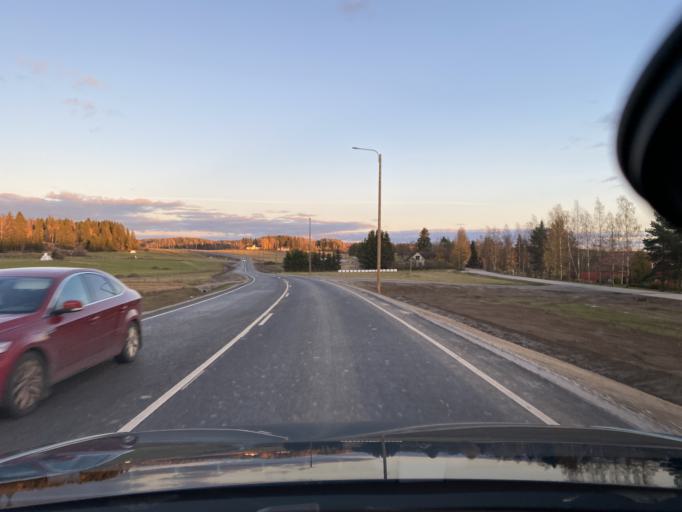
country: FI
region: Pirkanmaa
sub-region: Tampere
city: Vesilahti
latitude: 61.2895
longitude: 23.6080
